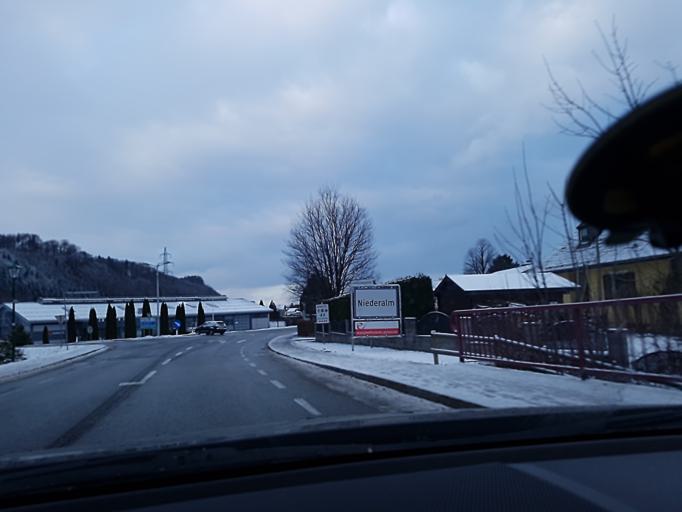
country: AT
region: Salzburg
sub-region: Politischer Bezirk Salzburg-Umgebung
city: Anif
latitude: 47.7240
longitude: 13.0599
